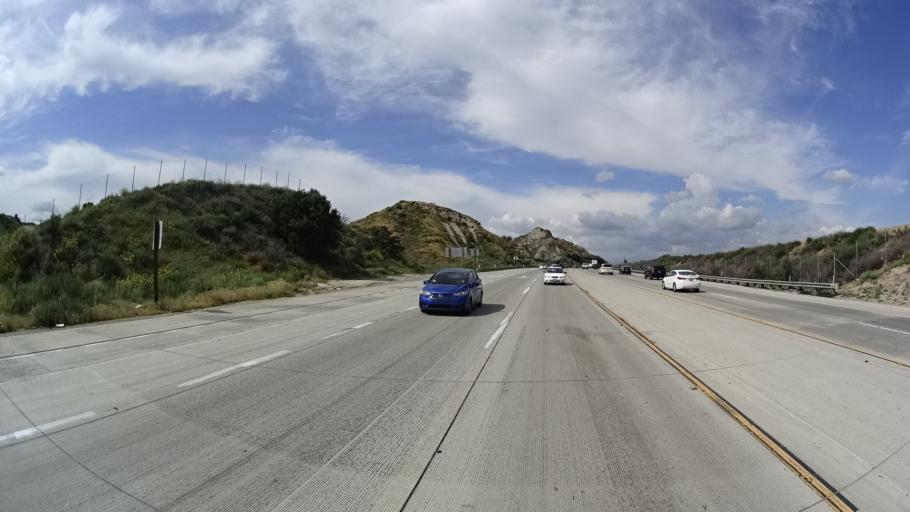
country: US
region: California
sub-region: Riverside County
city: Corona
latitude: 33.8904
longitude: -117.6466
